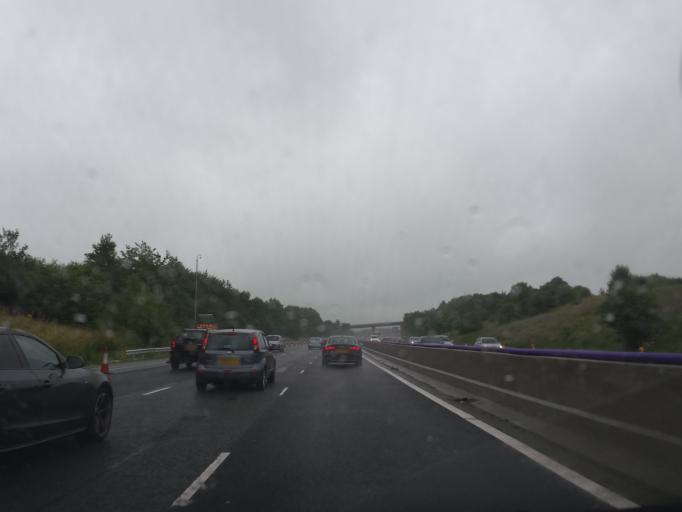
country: GB
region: England
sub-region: Derbyshire
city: Tibshelf
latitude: 53.1684
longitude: -1.3243
